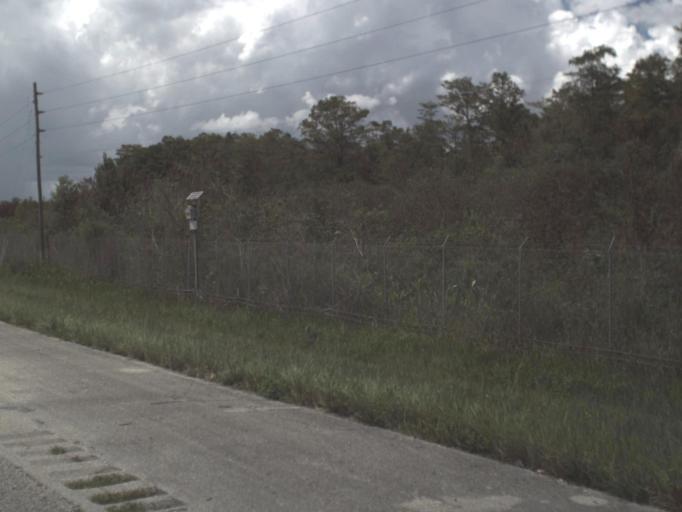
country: US
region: Florida
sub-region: Collier County
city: Immokalee
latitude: 26.1560
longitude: -81.2588
